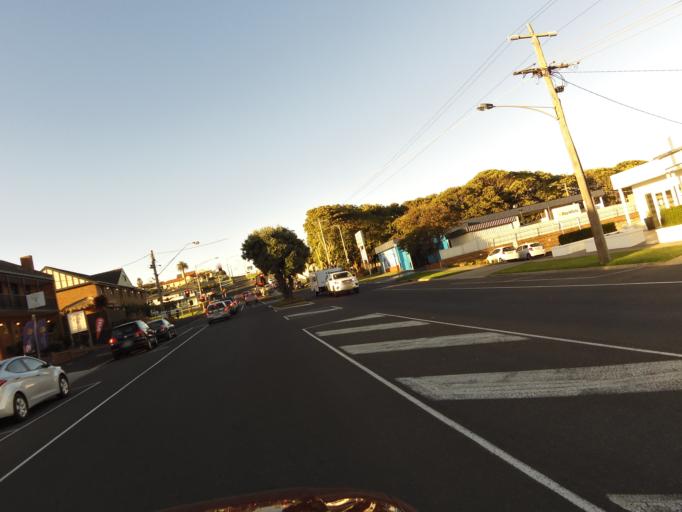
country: AU
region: Victoria
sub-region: Warrnambool
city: Warrnambool
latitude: -38.3826
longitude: 142.4874
